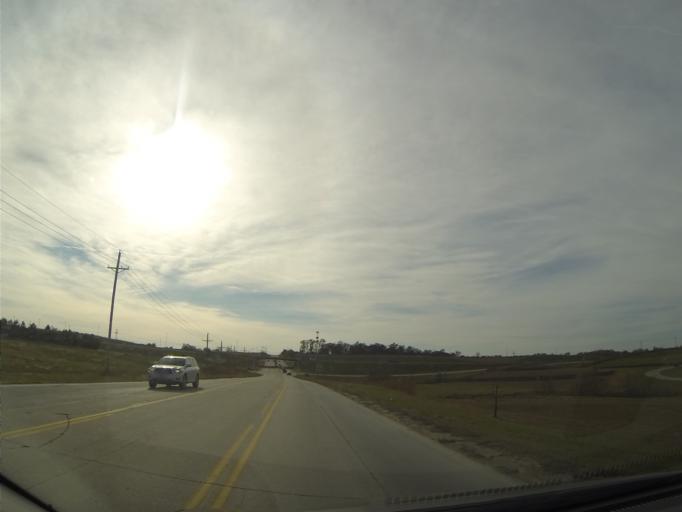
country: US
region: Nebraska
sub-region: Douglas County
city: Elkhorn
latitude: 41.2659
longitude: -96.2156
